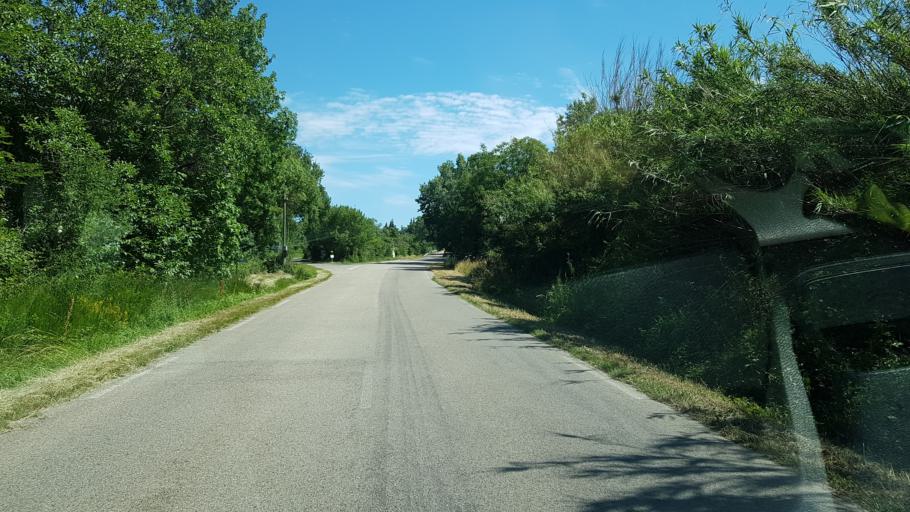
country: FR
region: Provence-Alpes-Cote d'Azur
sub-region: Departement des Bouches-du-Rhone
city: Saint-Martin-de-Crau
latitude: 43.6342
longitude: 4.7468
